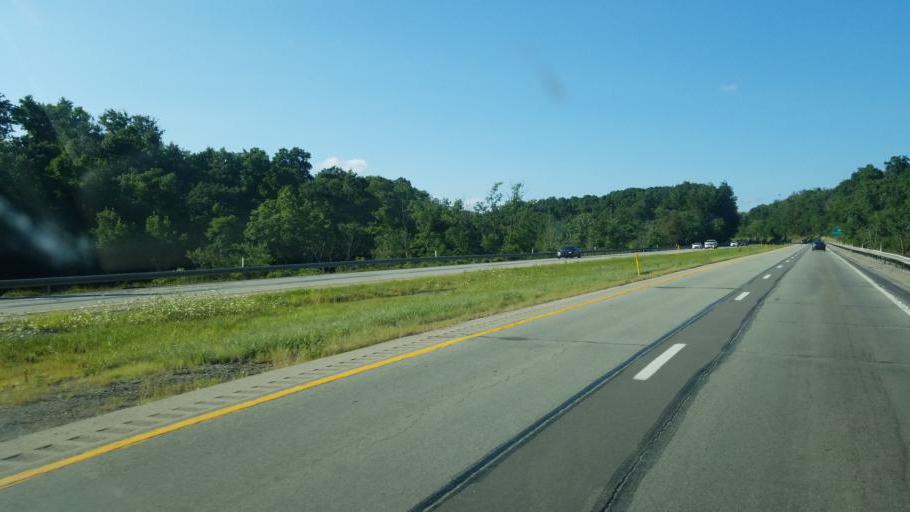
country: US
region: Pennsylvania
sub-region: Washington County
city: East Washington
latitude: 40.1333
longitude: -80.2083
